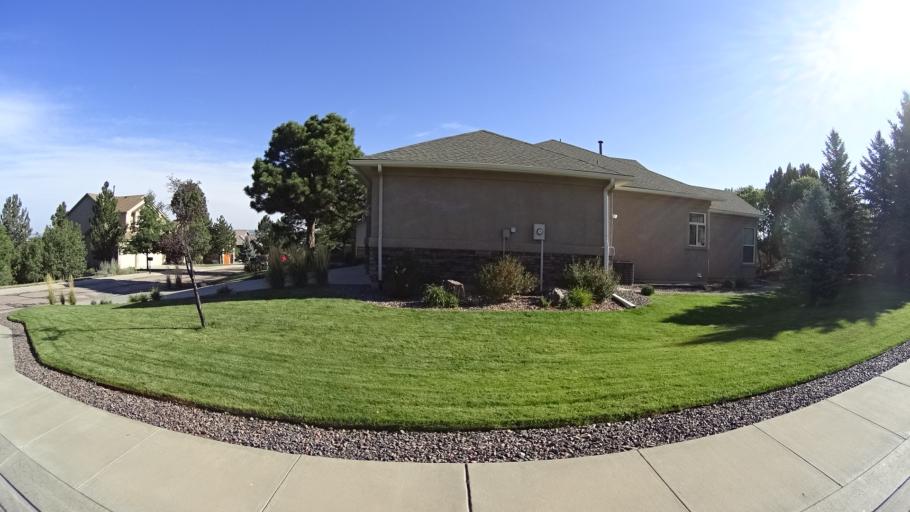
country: US
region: Colorado
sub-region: El Paso County
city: Colorado Springs
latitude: 38.9014
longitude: -104.7936
